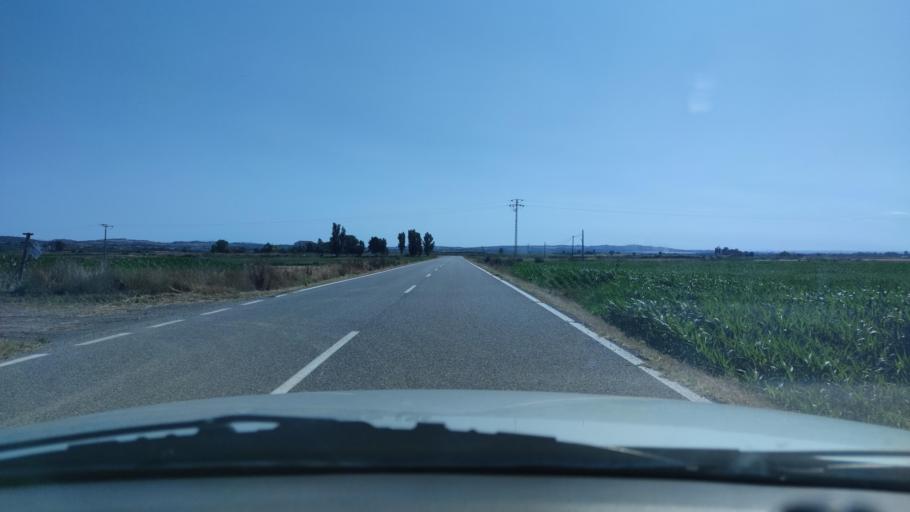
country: ES
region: Catalonia
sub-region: Provincia de Lleida
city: Bellcaire d'Urgell
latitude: 41.7367
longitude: 0.9415
